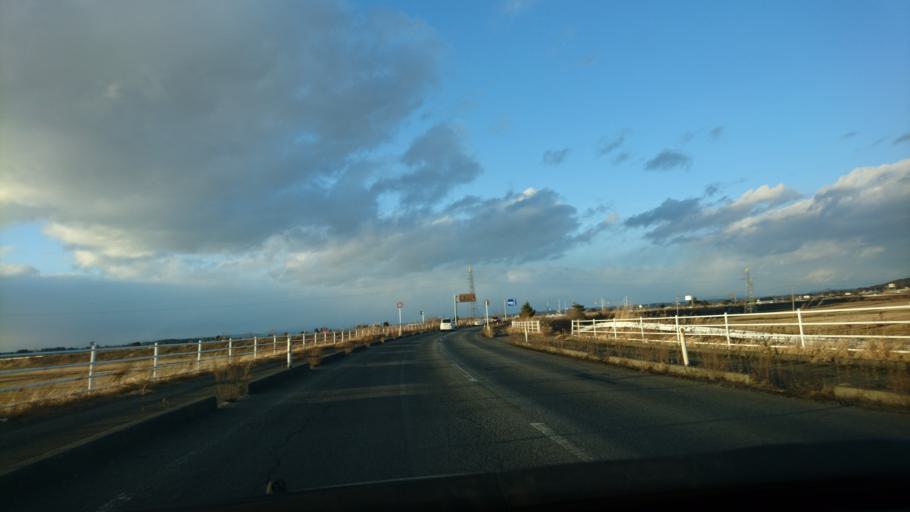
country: JP
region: Miyagi
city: Wakuya
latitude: 38.7249
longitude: 141.1487
